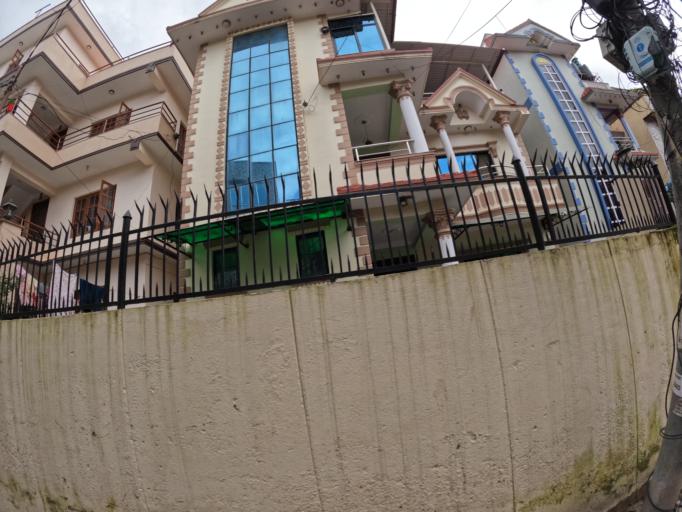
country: NP
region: Central Region
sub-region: Bagmati Zone
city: Kathmandu
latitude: 27.7390
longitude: 85.3182
